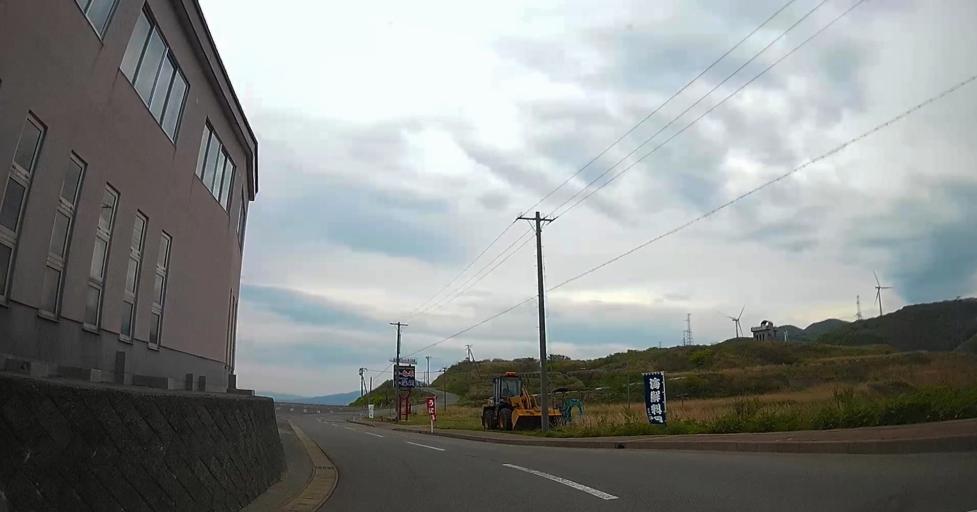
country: JP
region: Aomori
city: Shimokizukuri
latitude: 41.2571
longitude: 140.3468
